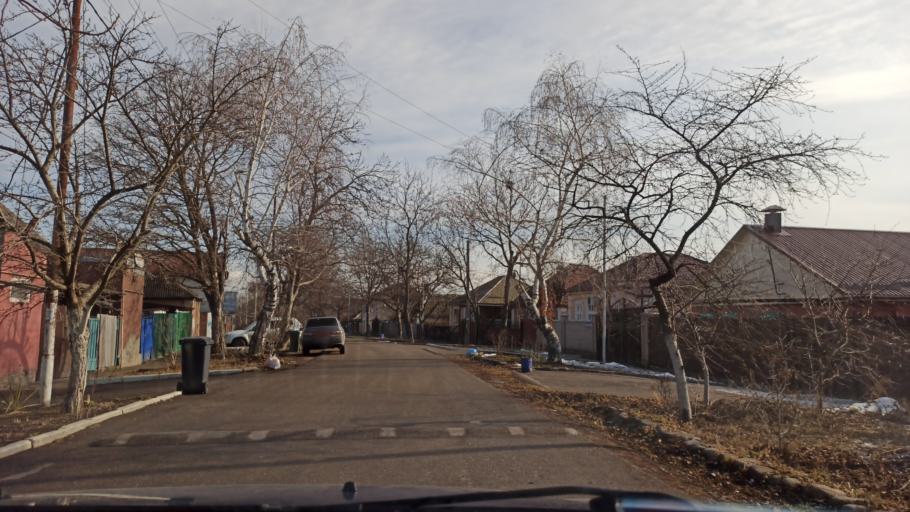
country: RU
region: Stavropol'skiy
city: Yessentukskaya
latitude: 44.0390
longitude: 42.8781
